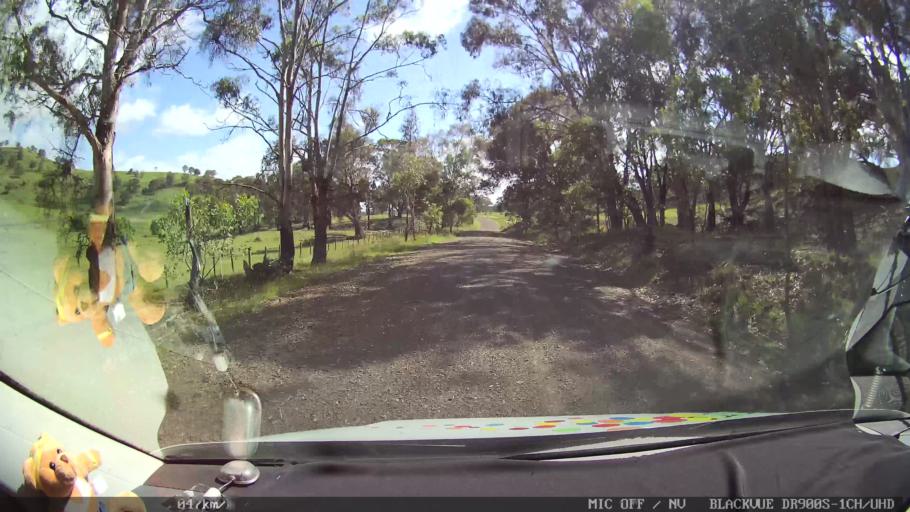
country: AU
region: New South Wales
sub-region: Guyra
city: Guyra
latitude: -29.9911
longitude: 151.6864
